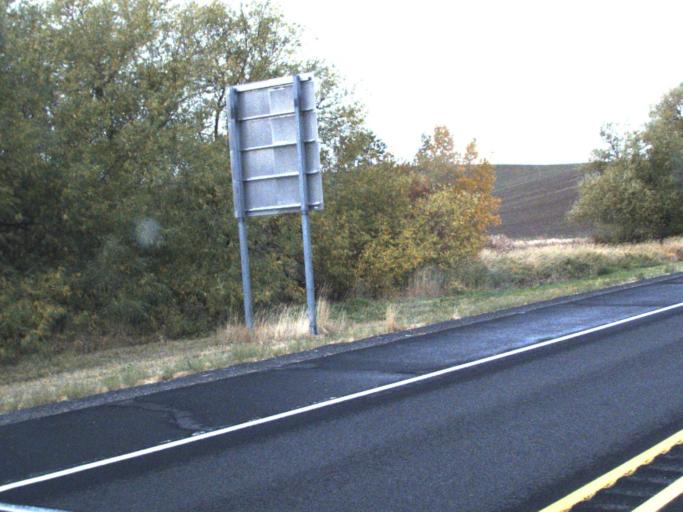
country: US
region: Washington
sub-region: Whitman County
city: Pullman
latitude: 46.7409
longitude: -117.2310
